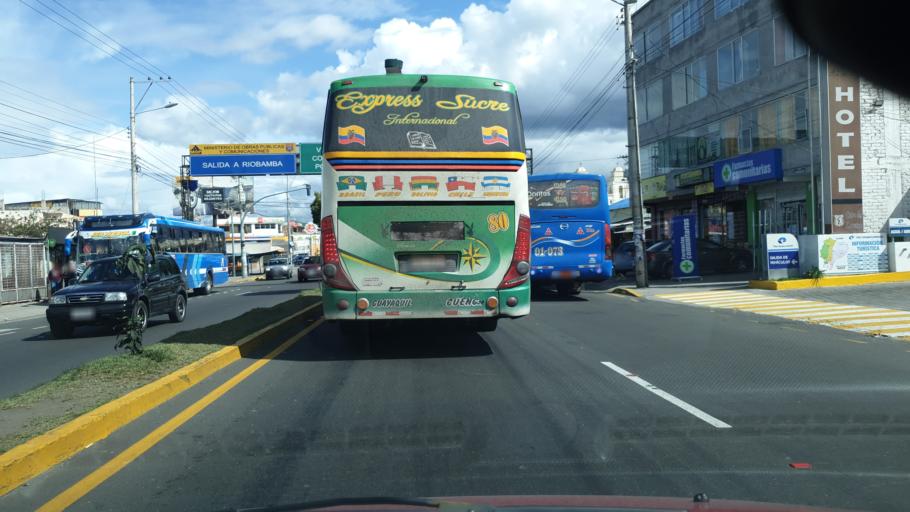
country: EC
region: Tungurahua
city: Ambato
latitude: -1.3058
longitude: -78.6370
